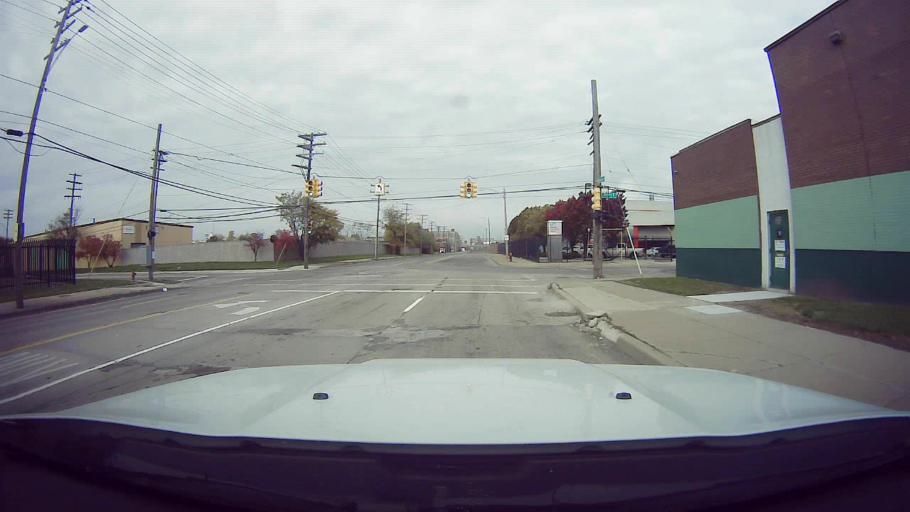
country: US
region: Michigan
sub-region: Wayne County
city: Hamtramck
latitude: 42.3660
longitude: -83.0534
